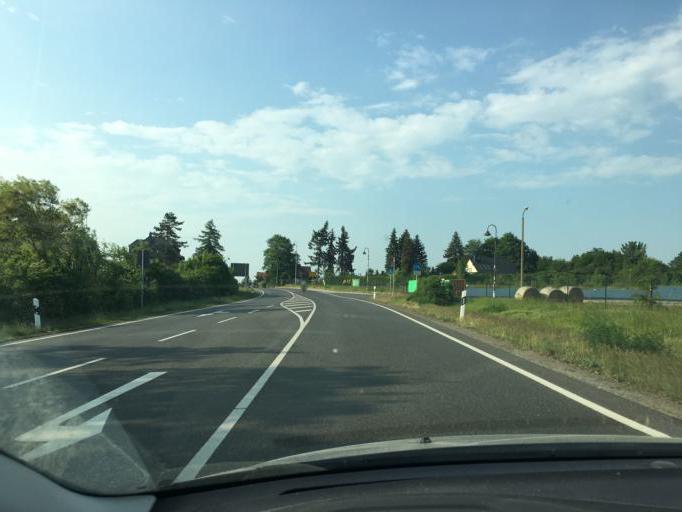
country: DE
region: Saxony
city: Grossbothen
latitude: 51.1800
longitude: 12.7611
